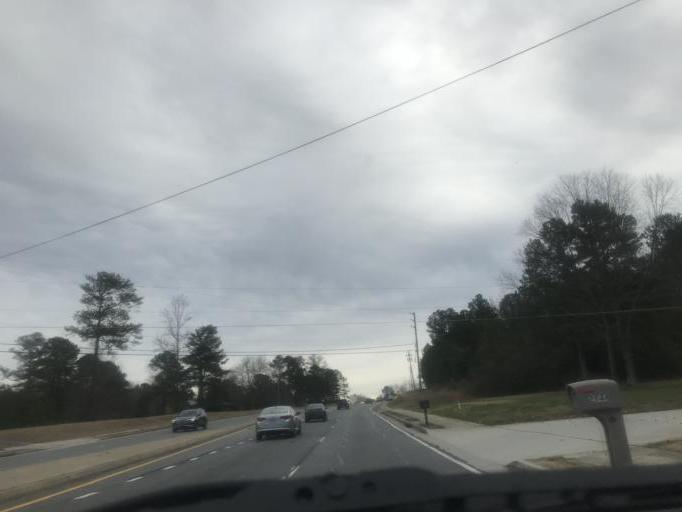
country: US
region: Georgia
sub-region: Gwinnett County
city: Buford
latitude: 34.0698
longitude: -83.9599
